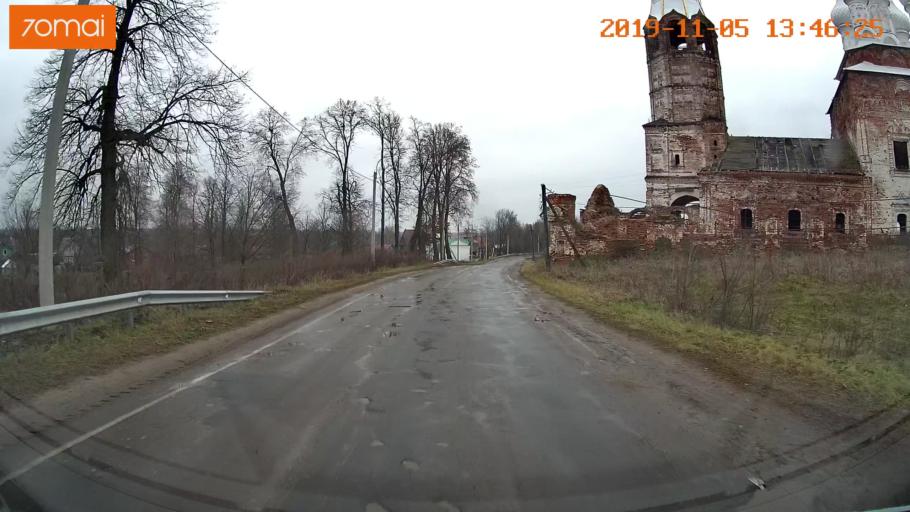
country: RU
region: Ivanovo
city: Shuya
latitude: 56.9952
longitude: 41.4100
